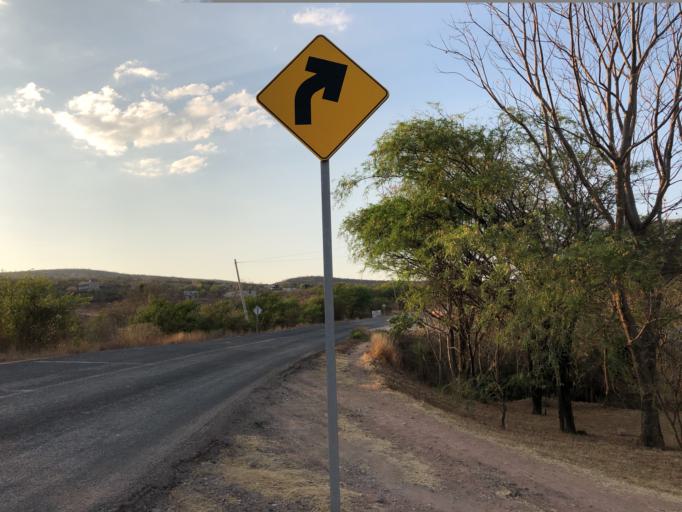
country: MX
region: Oaxaca
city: Ciudad de Huajuapam de Leon
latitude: 17.8371
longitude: -97.7914
